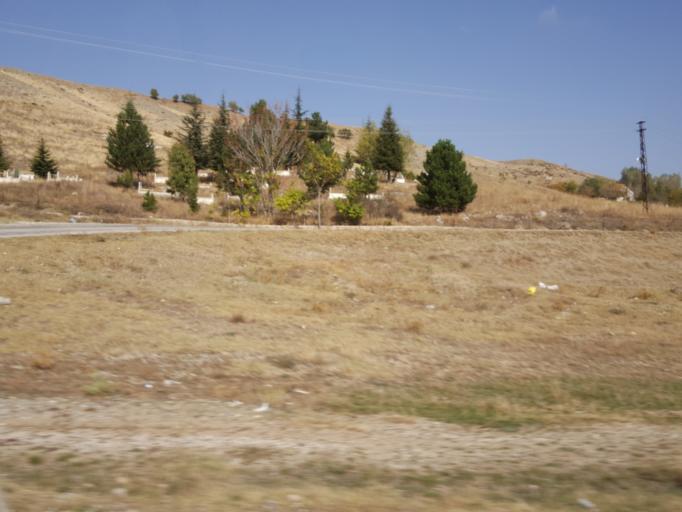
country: TR
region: Corum
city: Bogazkale
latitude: 40.1587
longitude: 34.6368
